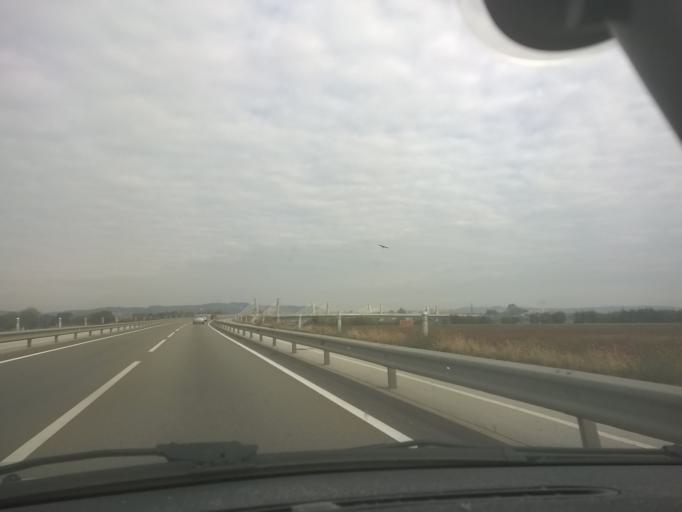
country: SI
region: Ptuj
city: Ptuj
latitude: 46.4098
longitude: 15.8769
